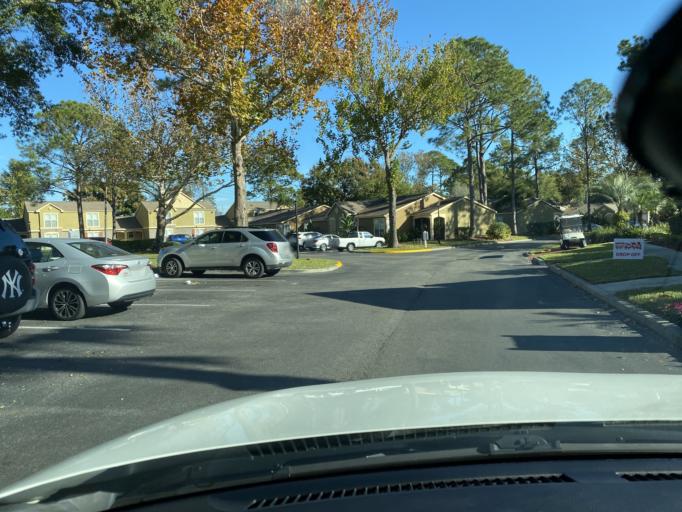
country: US
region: Florida
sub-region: Orange County
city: Azalea Park
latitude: 28.5181
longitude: -81.3081
